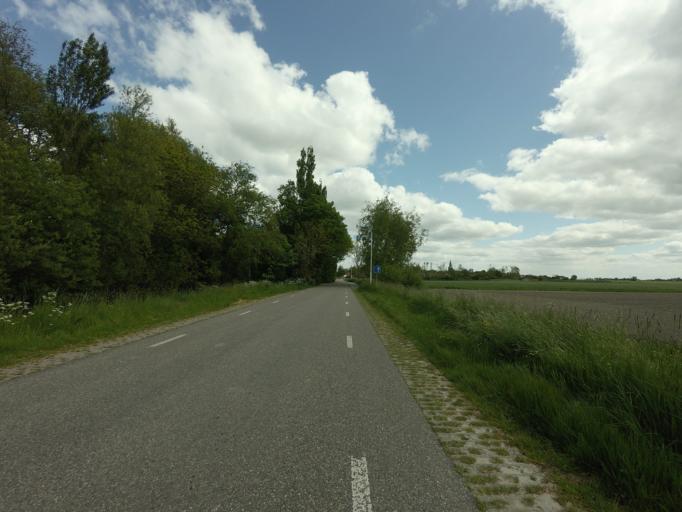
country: NL
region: Friesland
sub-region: Sudwest Fryslan
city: Bolsward
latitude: 53.0904
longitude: 5.5416
